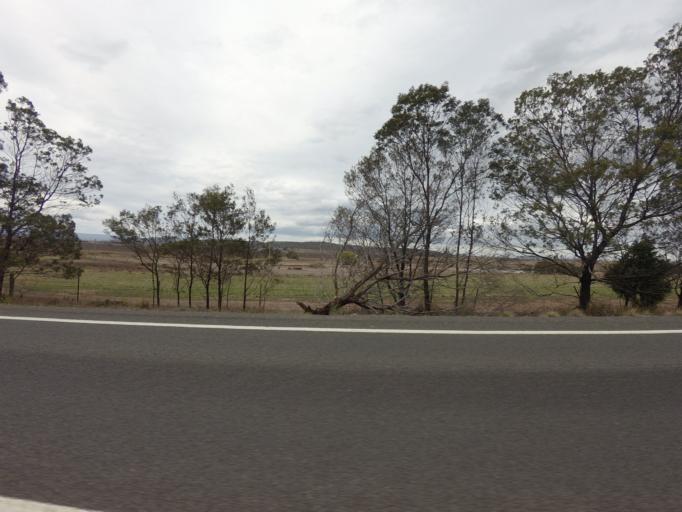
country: AU
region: Tasmania
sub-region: Break O'Day
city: St Helens
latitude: -42.0777
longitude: 148.0682
